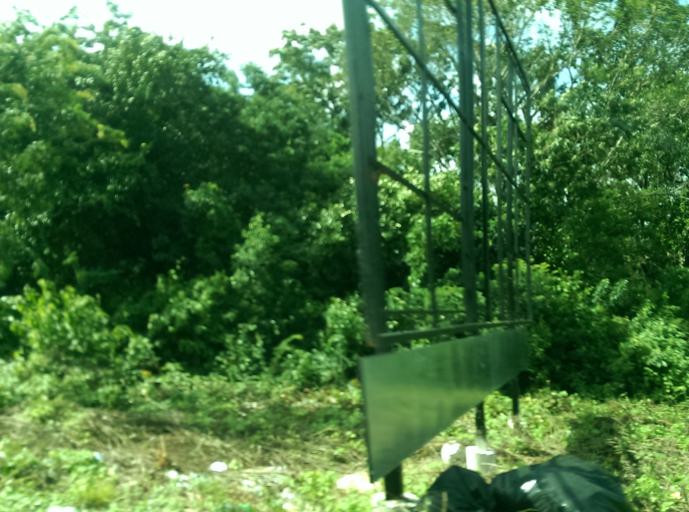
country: MX
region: Quintana Roo
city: Tulum
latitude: 20.2167
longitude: -87.4543
